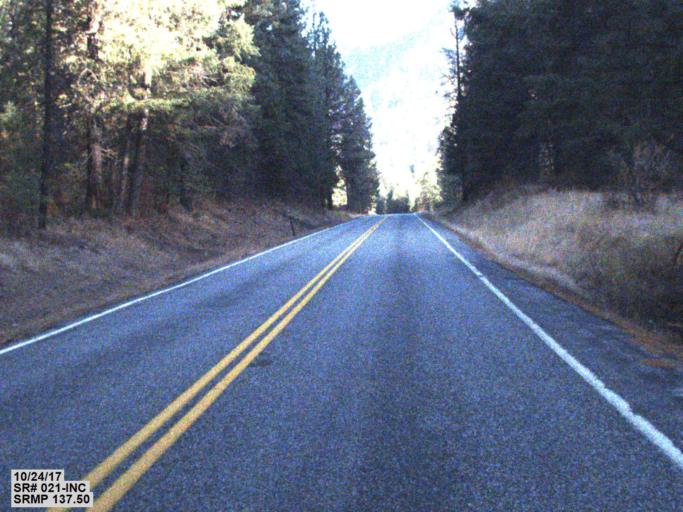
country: US
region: Washington
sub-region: Ferry County
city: Republic
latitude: 48.3553
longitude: -118.7426
